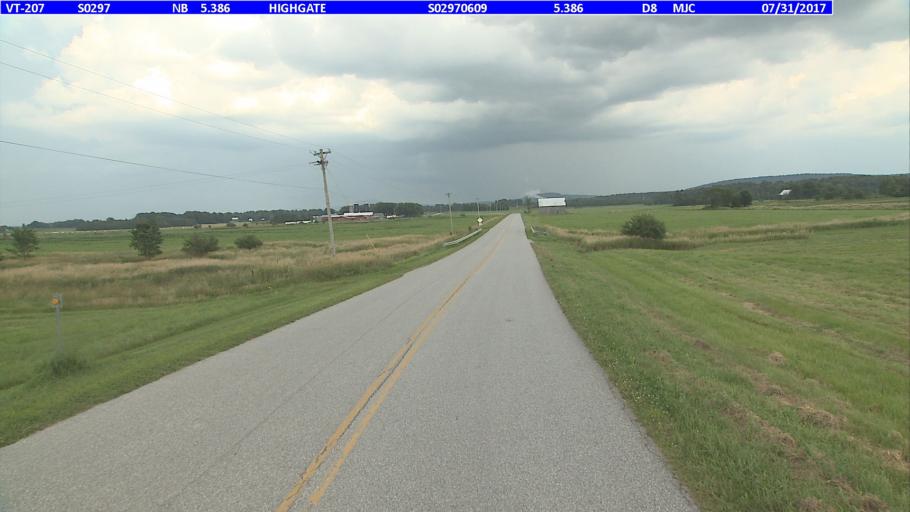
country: CA
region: Quebec
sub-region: Monteregie
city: Bedford
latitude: 45.0055
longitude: -72.9989
